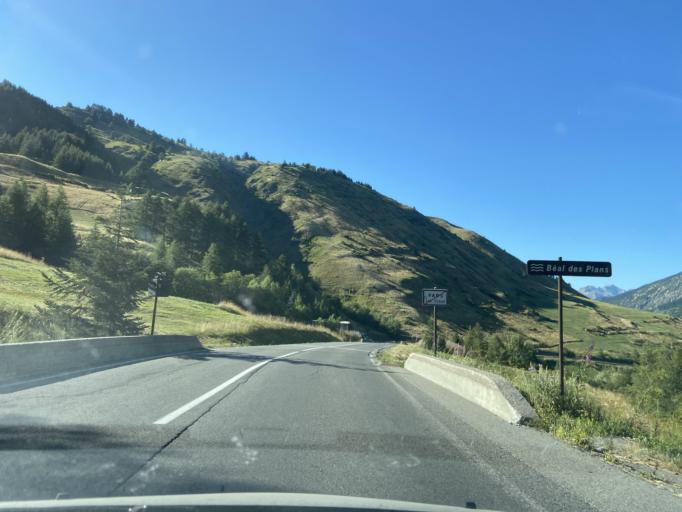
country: FR
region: Provence-Alpes-Cote d'Azur
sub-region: Departement des Hautes-Alpes
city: Guillestre
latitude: 44.5812
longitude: 6.6841
